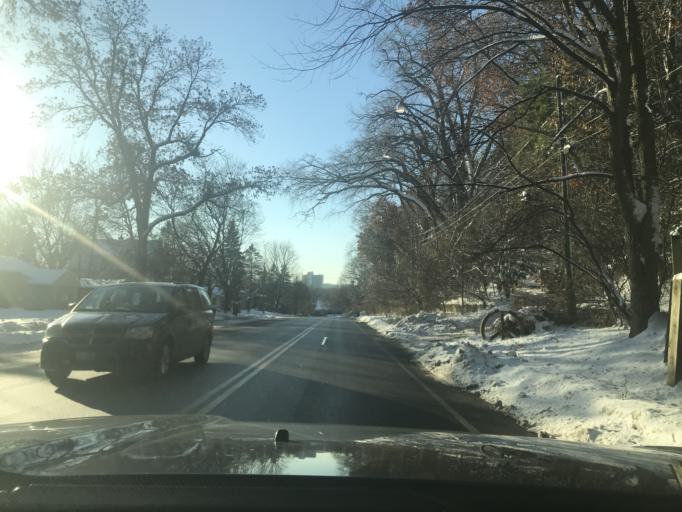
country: US
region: Minnesota
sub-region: Dakota County
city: Mendota Heights
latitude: 44.9223
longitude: -93.1467
